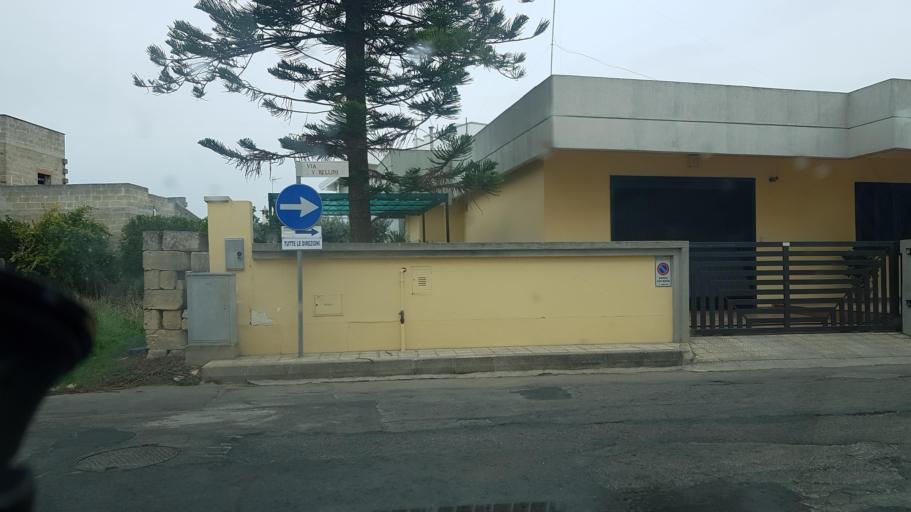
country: IT
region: Apulia
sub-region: Provincia di Lecce
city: Leverano
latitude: 40.2939
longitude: 18.0016
